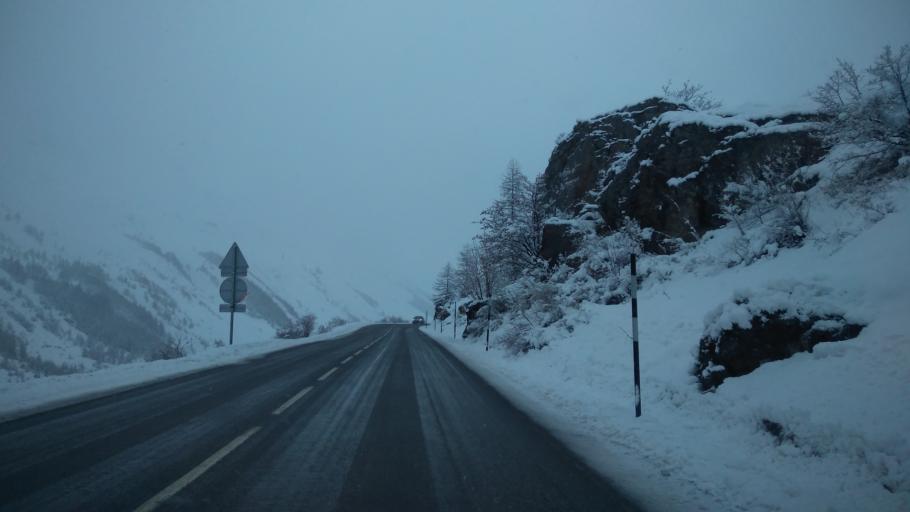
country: FR
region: Provence-Alpes-Cote d'Azur
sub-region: Departement des Hautes-Alpes
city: Le Monetier-les-Bains
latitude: 45.0206
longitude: 6.4608
